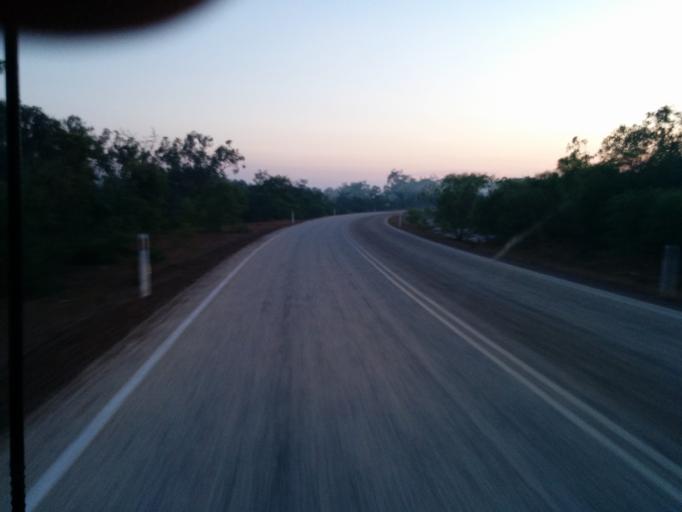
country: AU
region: Northern Territory
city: Alyangula
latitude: -13.8729
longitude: 136.7805
